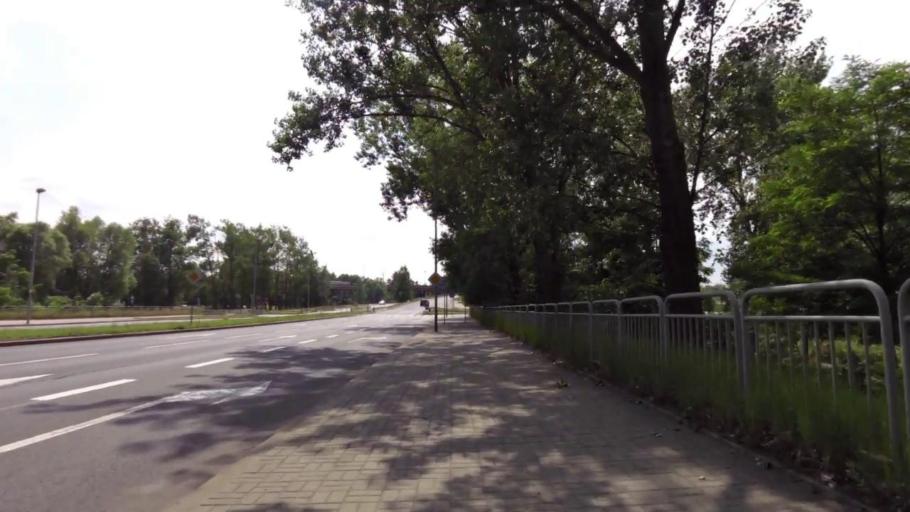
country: PL
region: West Pomeranian Voivodeship
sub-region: Szczecin
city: Szczecin
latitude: 53.3978
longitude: 14.6093
